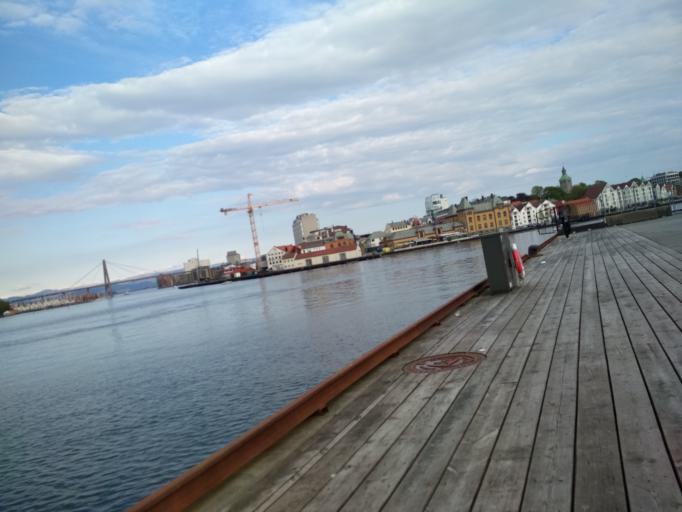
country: NO
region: Rogaland
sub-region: Stavanger
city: Stavanger
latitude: 58.9753
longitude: 5.7246
